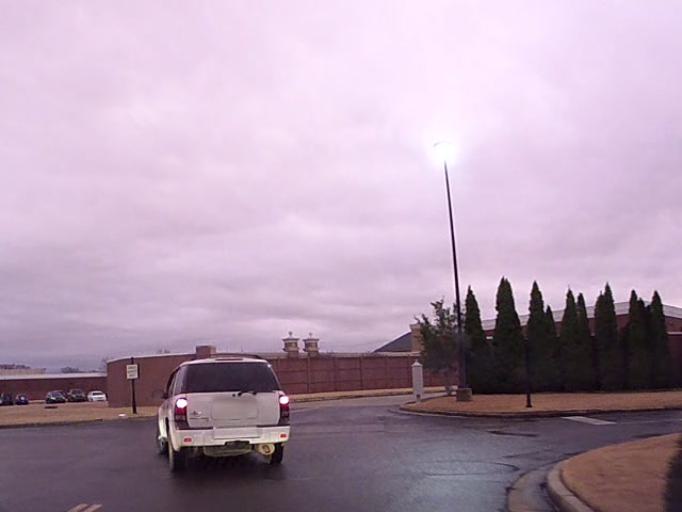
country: US
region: Tennessee
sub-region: Shelby County
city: Collierville
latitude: 35.0254
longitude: -89.7197
